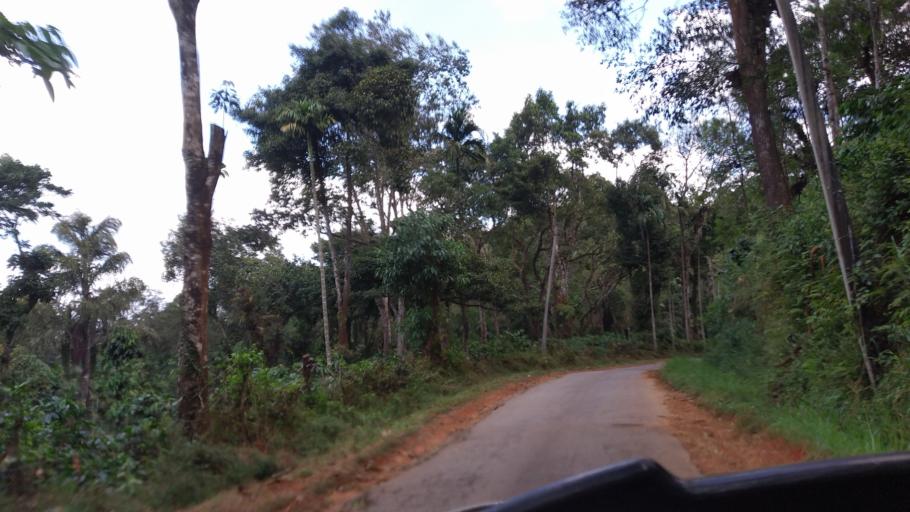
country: IN
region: Karnataka
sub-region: Kodagu
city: Ponnampet
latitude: 12.0372
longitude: 75.9095
